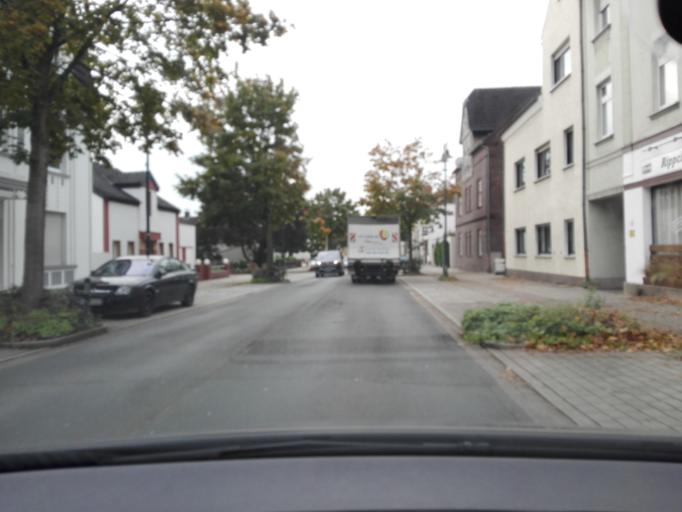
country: DE
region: North Rhine-Westphalia
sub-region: Regierungsbezirk Arnsberg
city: Holzwickede
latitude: 51.5085
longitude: 7.6171
